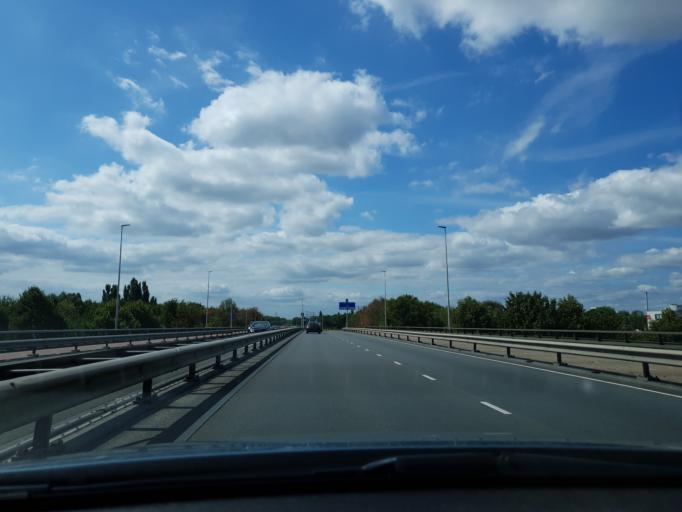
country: NL
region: Gelderland
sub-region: Gemeente Nijmegen
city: Lindenholt
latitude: 51.8372
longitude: 5.8091
